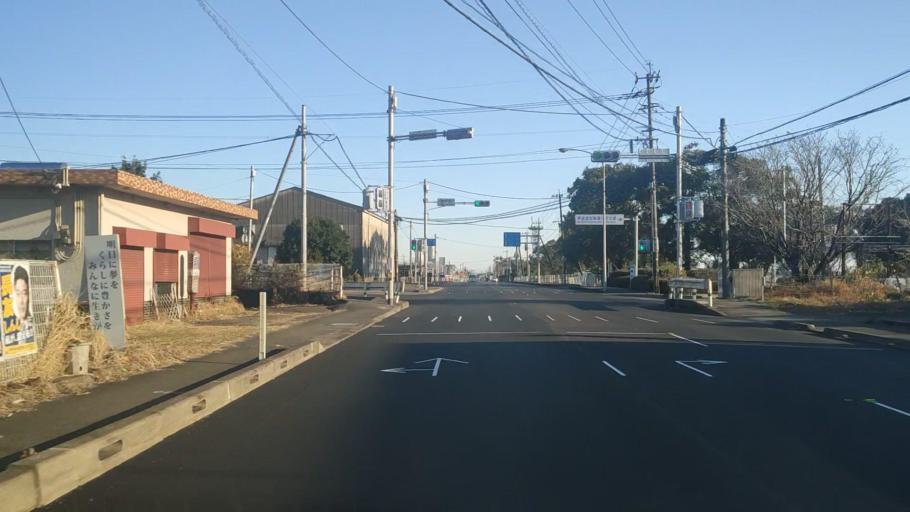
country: JP
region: Miyazaki
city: Takanabe
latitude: 32.2208
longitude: 131.5416
